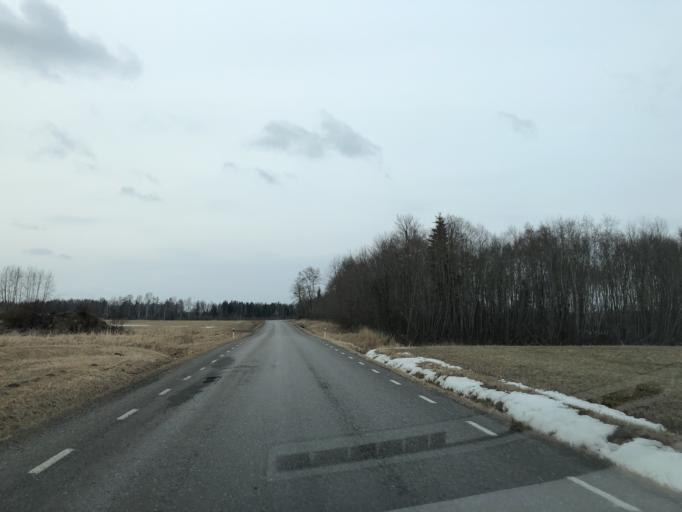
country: EE
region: Paernumaa
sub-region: Vaendra vald (alev)
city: Vandra
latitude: 58.6696
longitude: 25.0139
